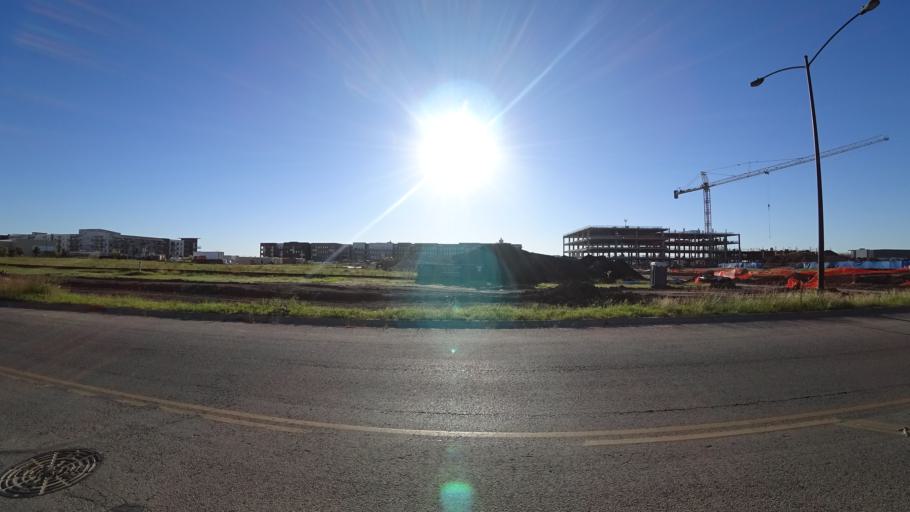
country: US
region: Texas
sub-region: Travis County
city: Austin
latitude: 30.3029
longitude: -97.7047
